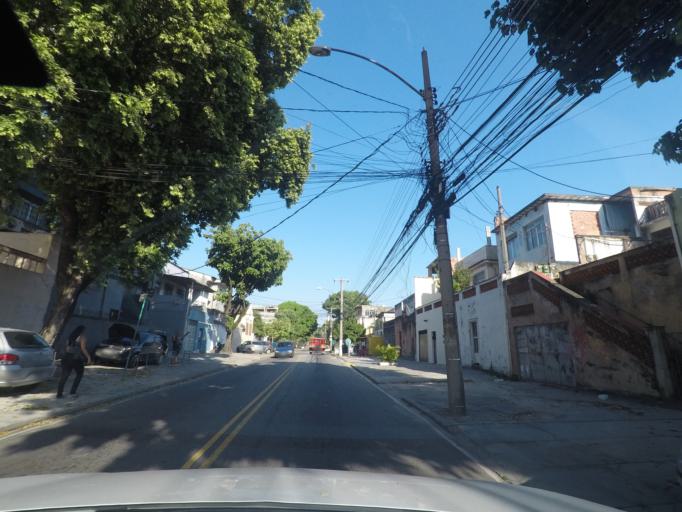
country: BR
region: Rio de Janeiro
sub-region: Duque De Caxias
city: Duque de Caxias
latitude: -22.8320
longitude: -43.2804
